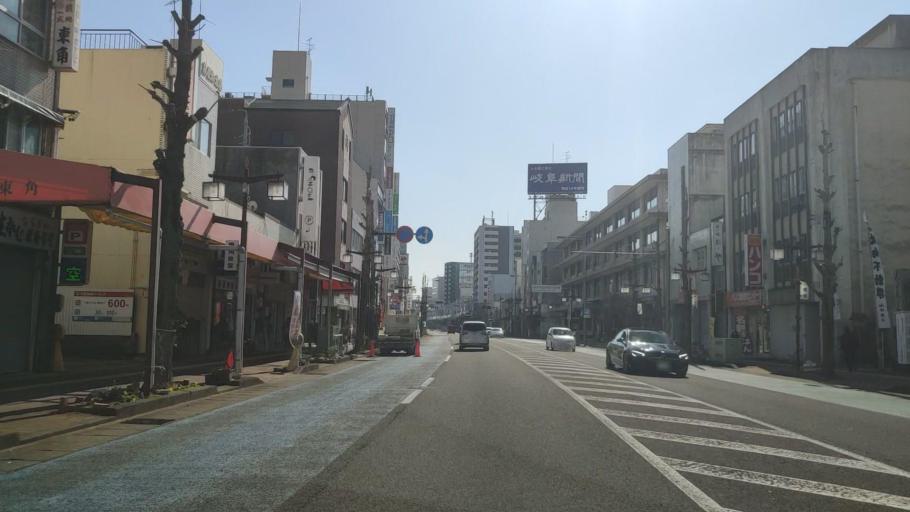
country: JP
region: Gifu
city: Gifu-shi
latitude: 35.4221
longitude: 136.7610
